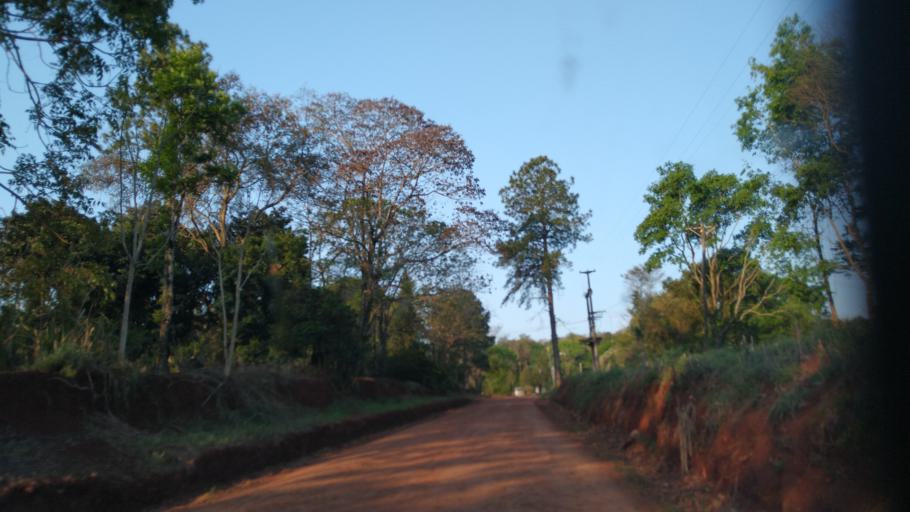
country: AR
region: Misiones
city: Jardin America
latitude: -27.0895
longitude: -55.2801
